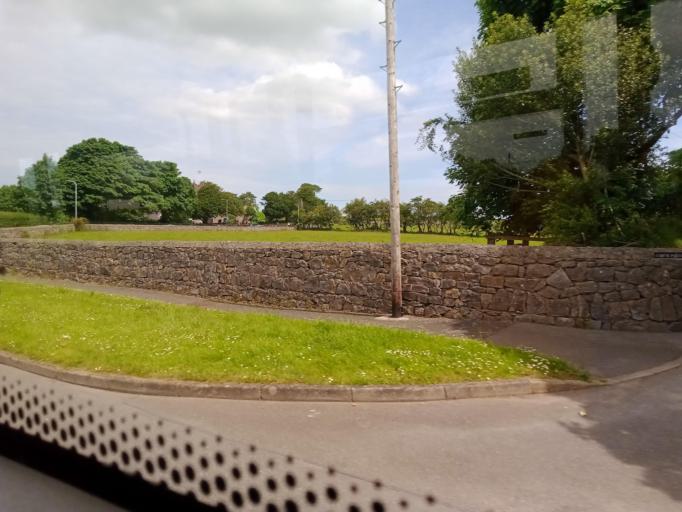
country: GB
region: Wales
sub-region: Anglesey
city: Menai Bridge
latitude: 53.2455
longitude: -4.1536
